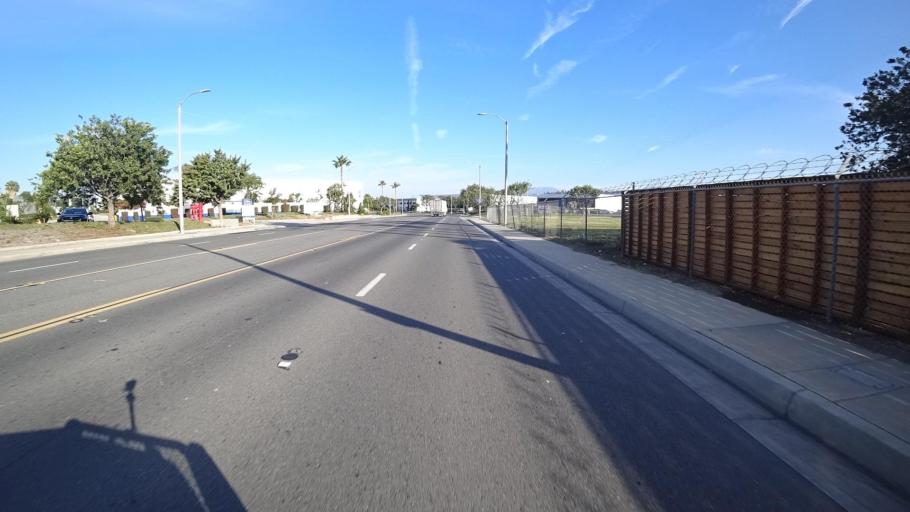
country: US
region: California
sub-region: Los Angeles County
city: South San Jose Hills
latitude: 34.0025
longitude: -117.9269
